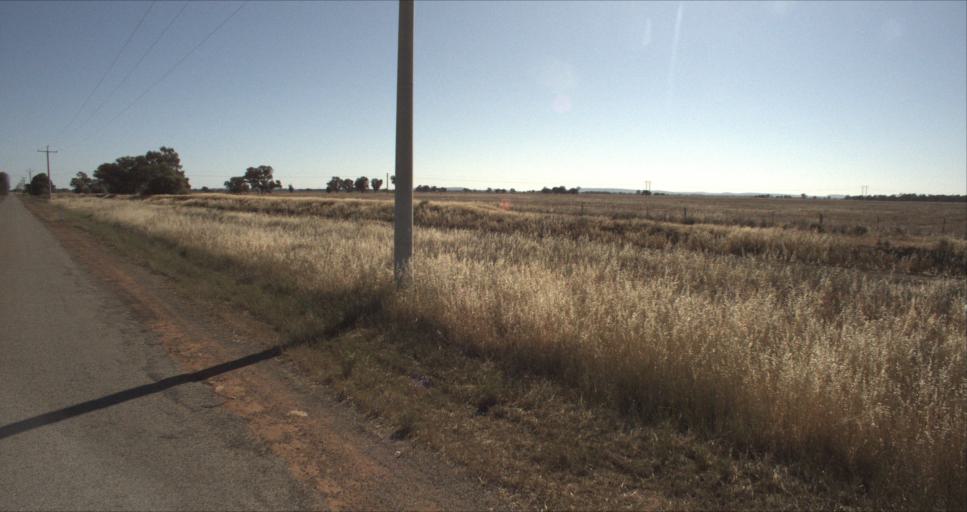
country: AU
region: New South Wales
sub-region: Leeton
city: Leeton
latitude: -34.5790
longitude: 146.3092
